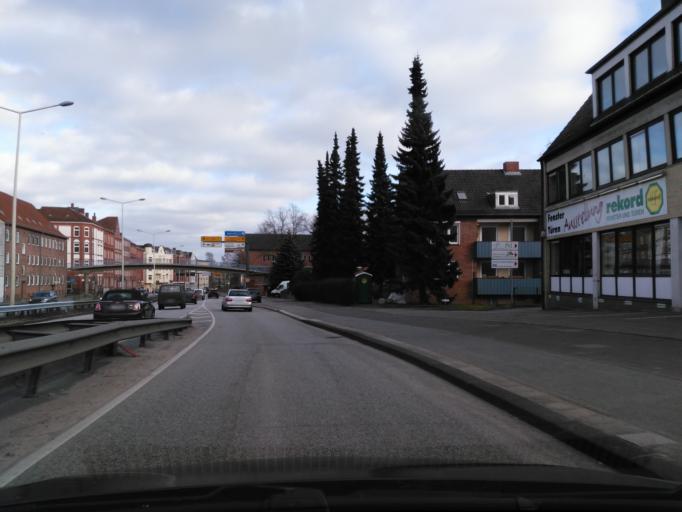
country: DE
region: Schleswig-Holstein
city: Kiel
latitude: 54.3043
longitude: 10.1202
